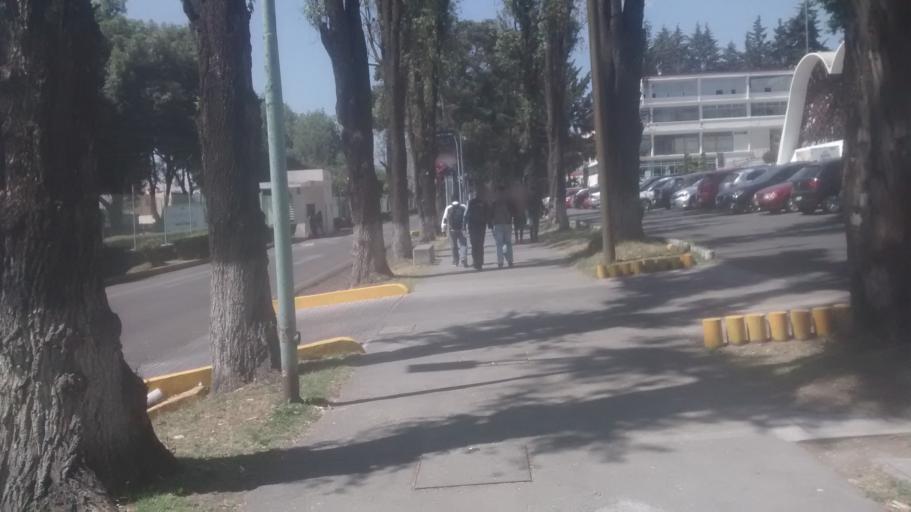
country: MX
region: Mexico
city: San Buenaventura
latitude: 19.2831
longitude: -99.6760
